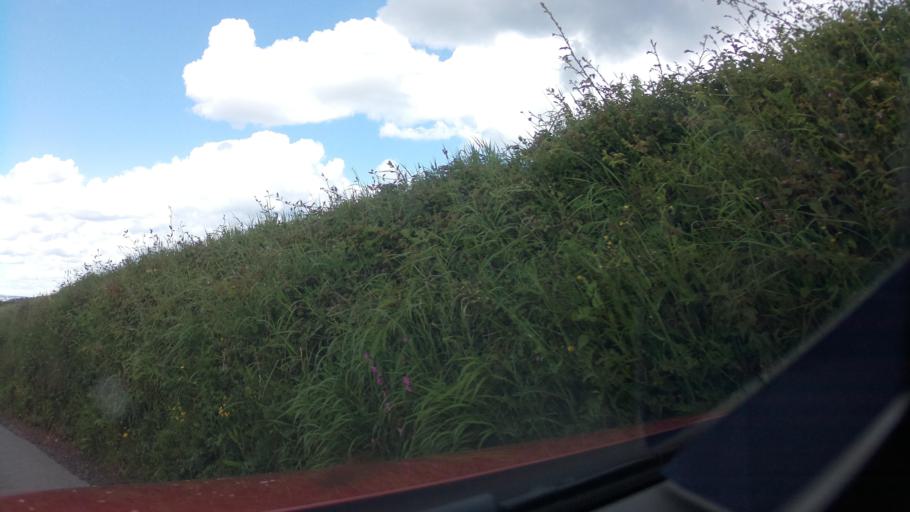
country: GB
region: England
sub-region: Devon
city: Dartmouth
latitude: 50.3516
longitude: -3.5375
